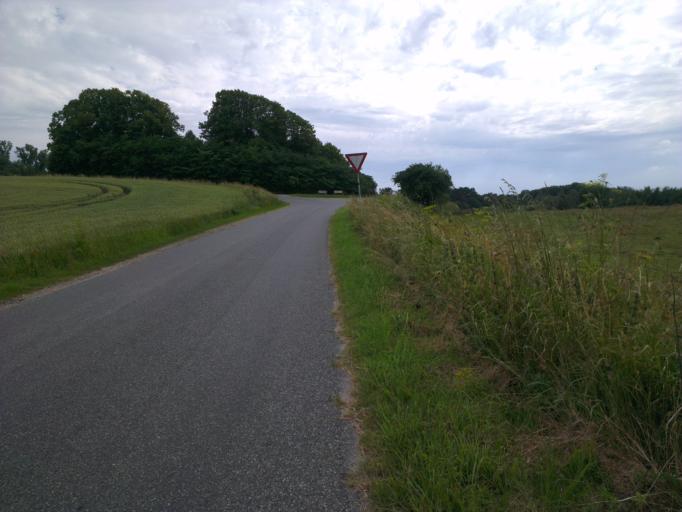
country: DK
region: Capital Region
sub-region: Frederikssund Kommune
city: Skibby
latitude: 55.7450
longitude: 12.0064
